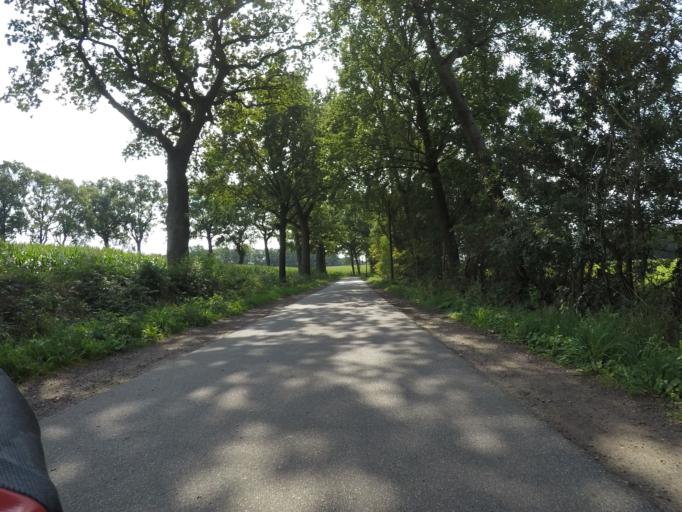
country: DE
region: Schleswig-Holstein
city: Henstedt-Ulzburg
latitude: 53.7617
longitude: 10.0247
